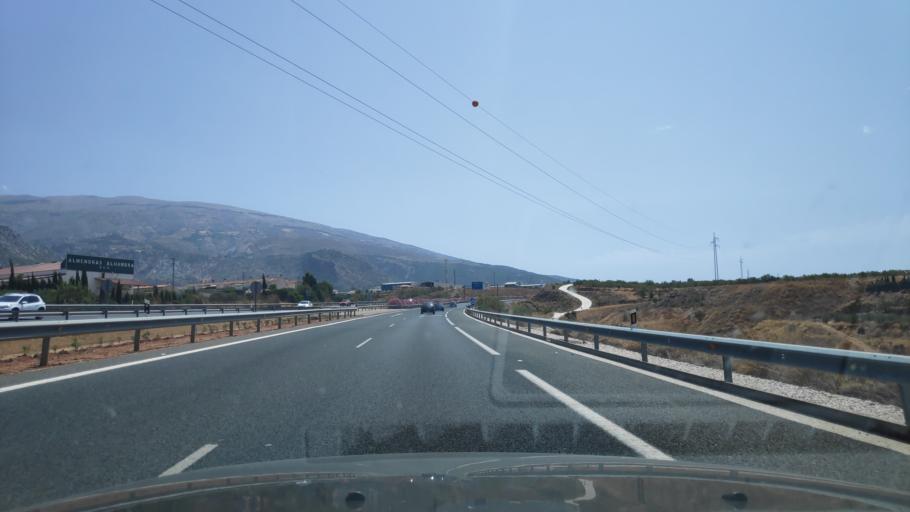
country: ES
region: Andalusia
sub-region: Provincia de Granada
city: Durcal
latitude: 36.9794
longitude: -3.5679
